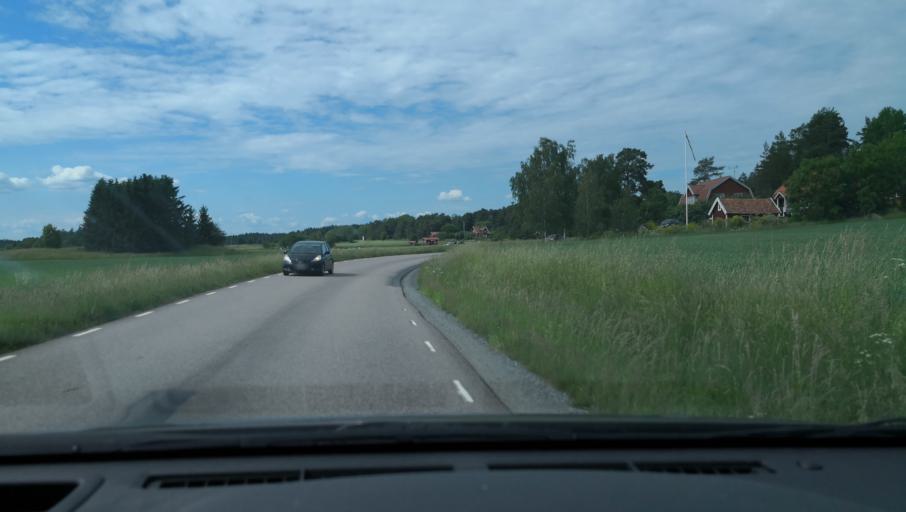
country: SE
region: Uppsala
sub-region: Uppsala Kommun
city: Uppsala
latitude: 59.8150
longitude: 17.5009
